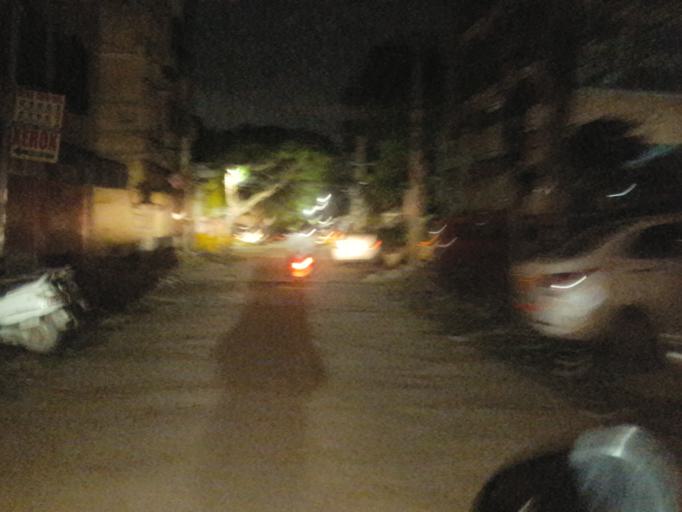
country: IN
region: Telangana
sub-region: Rangareddi
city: Kukatpalli
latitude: 17.4869
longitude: 78.3936
